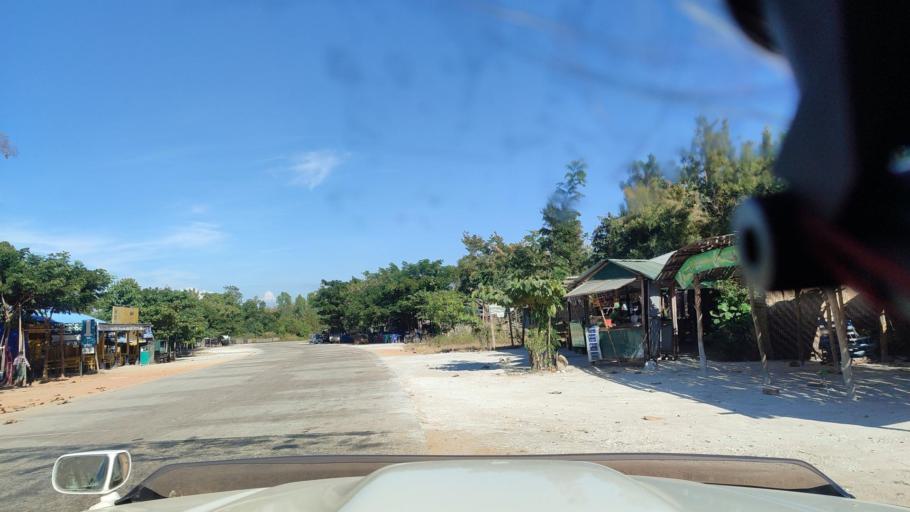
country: MM
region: Mandalay
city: Nay Pyi Taw
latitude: 19.9275
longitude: 95.9842
